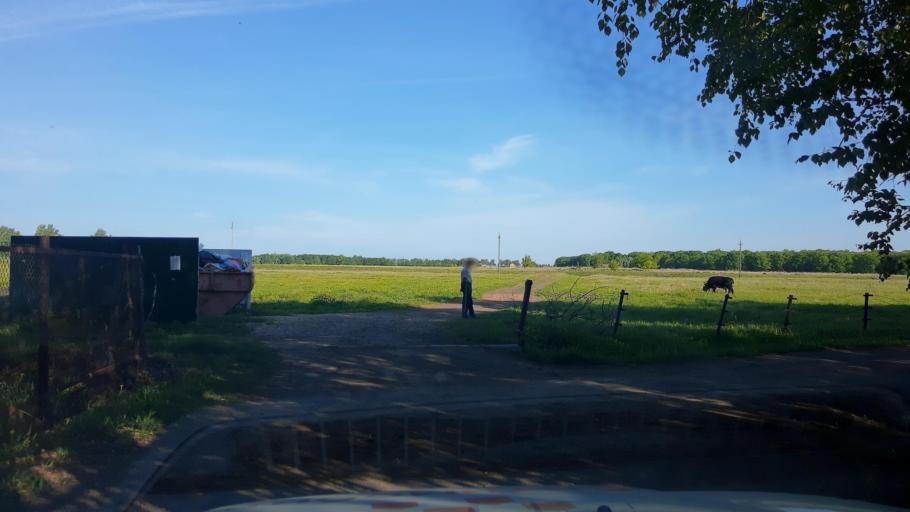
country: RU
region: Bashkortostan
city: Kabakovo
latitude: 54.4547
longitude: 55.9420
